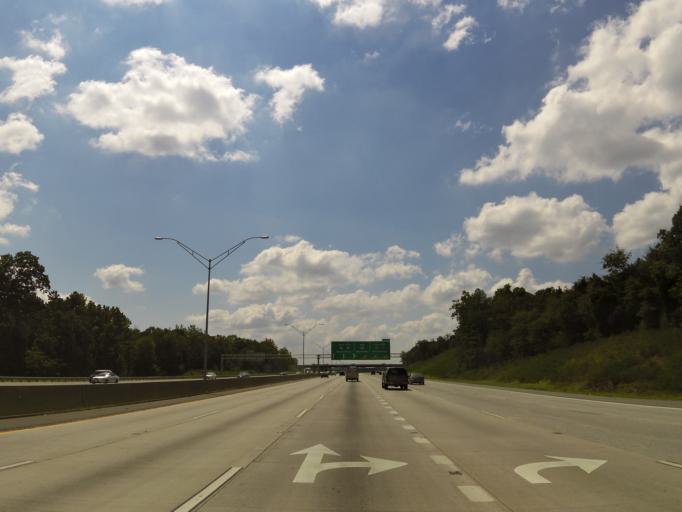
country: US
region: North Carolina
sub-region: Cabarrus County
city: Harrisburg
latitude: 35.3577
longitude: -80.7246
